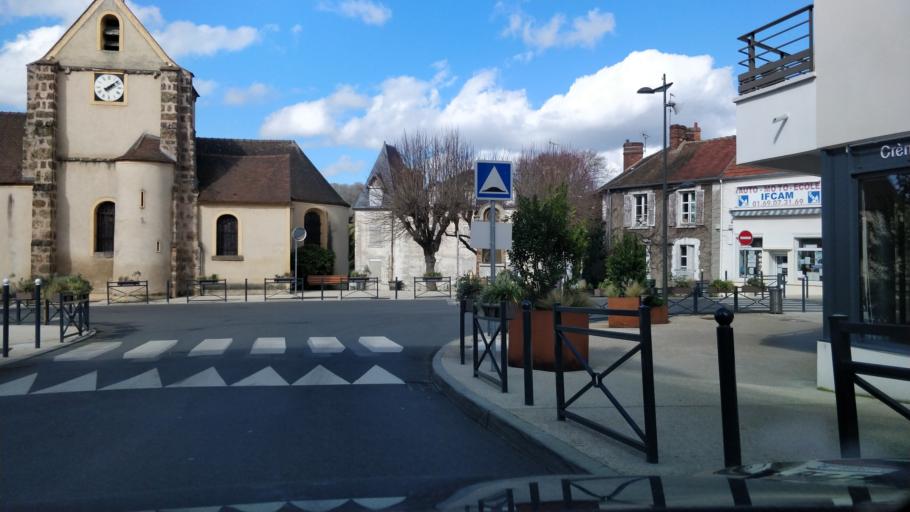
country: FR
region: Ile-de-France
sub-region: Departement de l'Essonne
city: Bures-sur-Yvette
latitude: 48.6966
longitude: 2.1624
